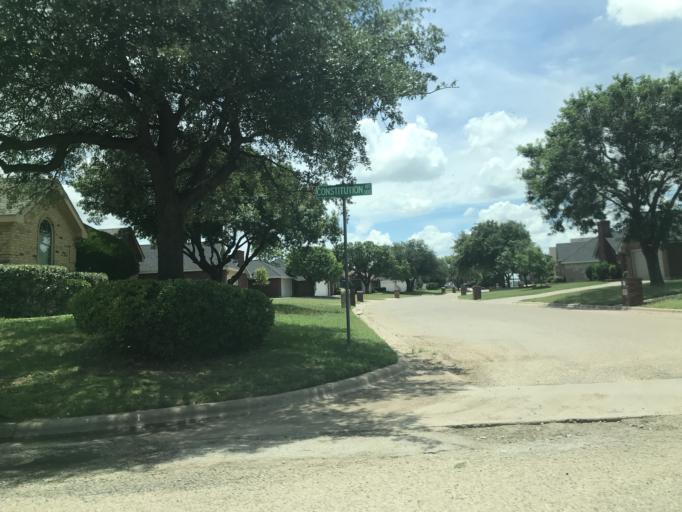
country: US
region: Texas
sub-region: Taylor County
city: Abilene
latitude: 32.4866
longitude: -99.6856
